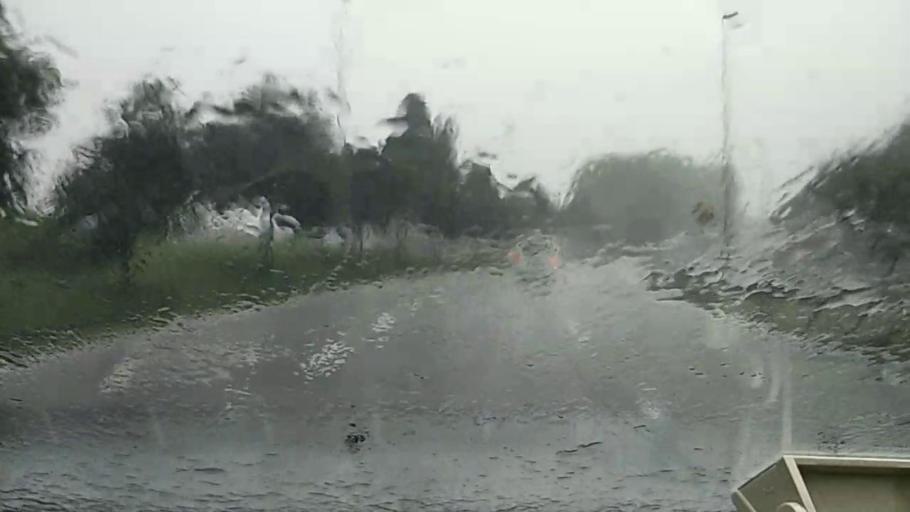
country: MY
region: Selangor
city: Kampong Baharu Balakong
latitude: 2.9820
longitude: 101.7629
